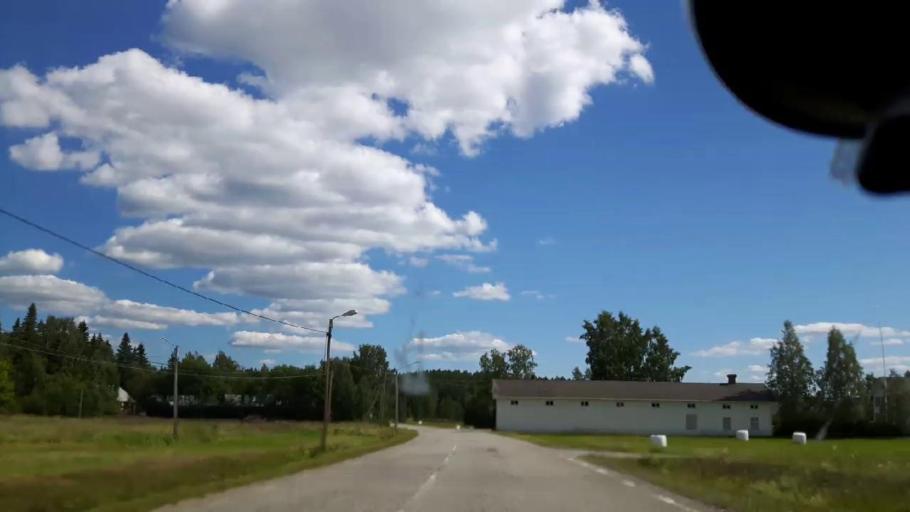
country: SE
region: Vaesternorrland
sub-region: Ange Kommun
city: Fransta
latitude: 62.7929
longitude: 16.2149
